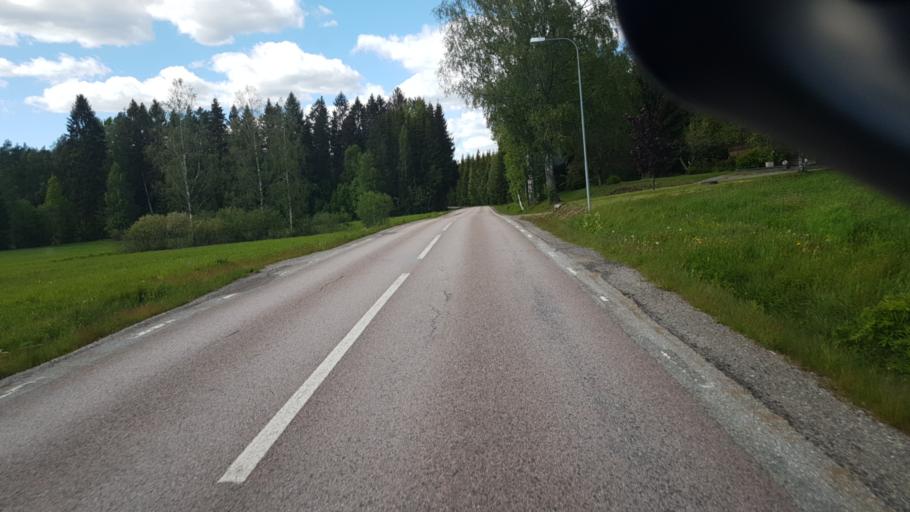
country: SE
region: Vaermland
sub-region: Sunne Kommun
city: Sunne
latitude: 59.6648
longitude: 13.0018
